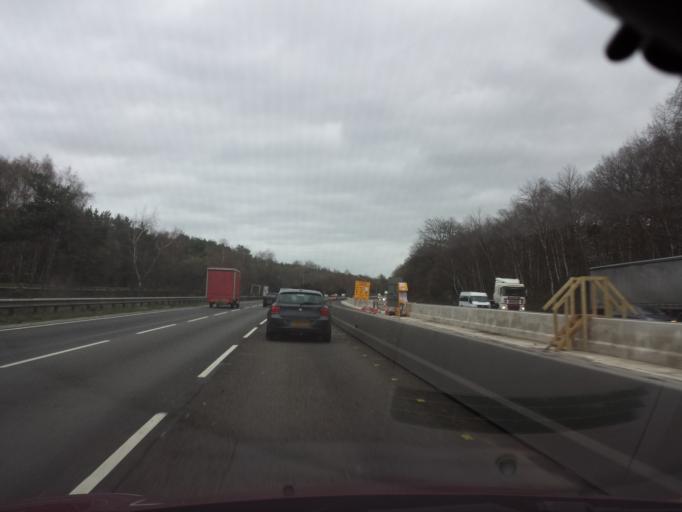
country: GB
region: England
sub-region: Surrey
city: Virginia Water
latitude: 51.3831
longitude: -0.5880
